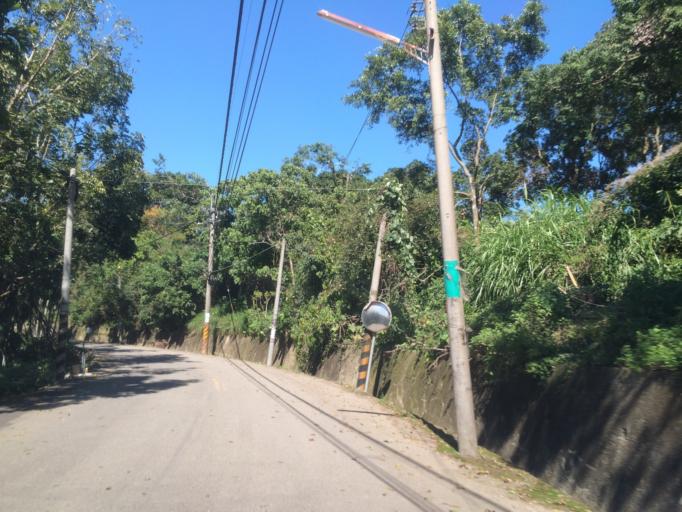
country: TW
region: Taiwan
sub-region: Yunlin
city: Douliu
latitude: 23.6937
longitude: 120.6220
